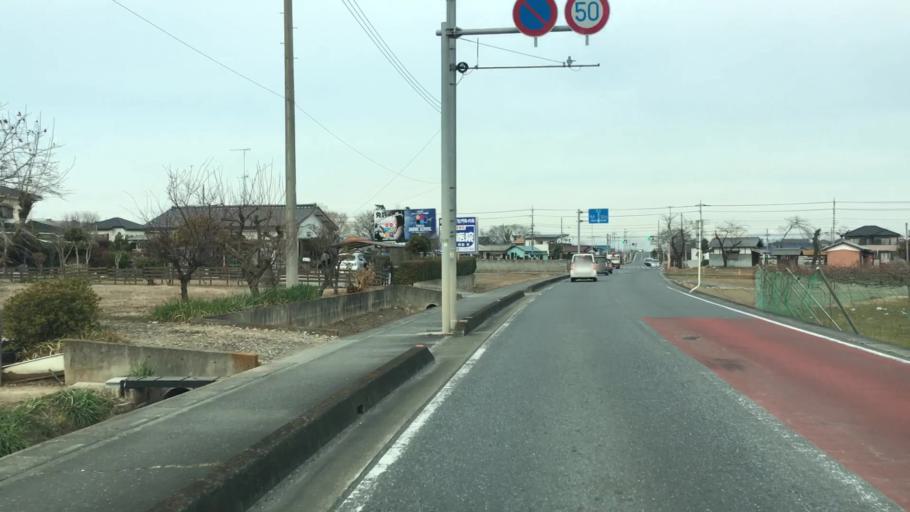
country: JP
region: Saitama
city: Kumagaya
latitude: 36.1295
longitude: 139.3239
